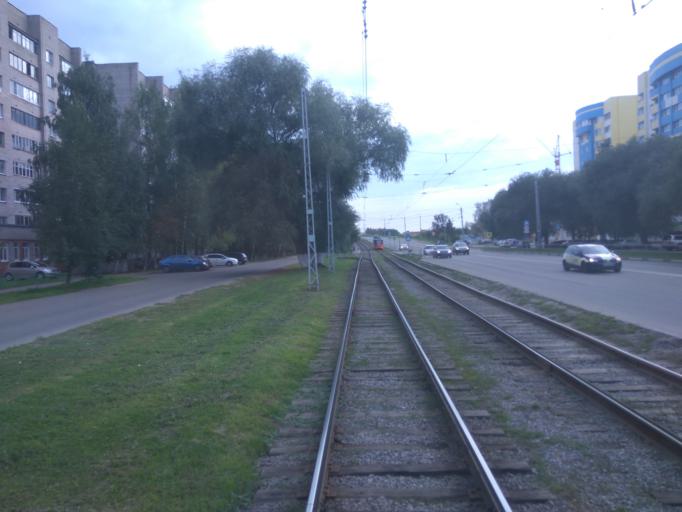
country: RU
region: Moskovskaya
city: Kolomna
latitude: 55.0754
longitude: 38.7611
